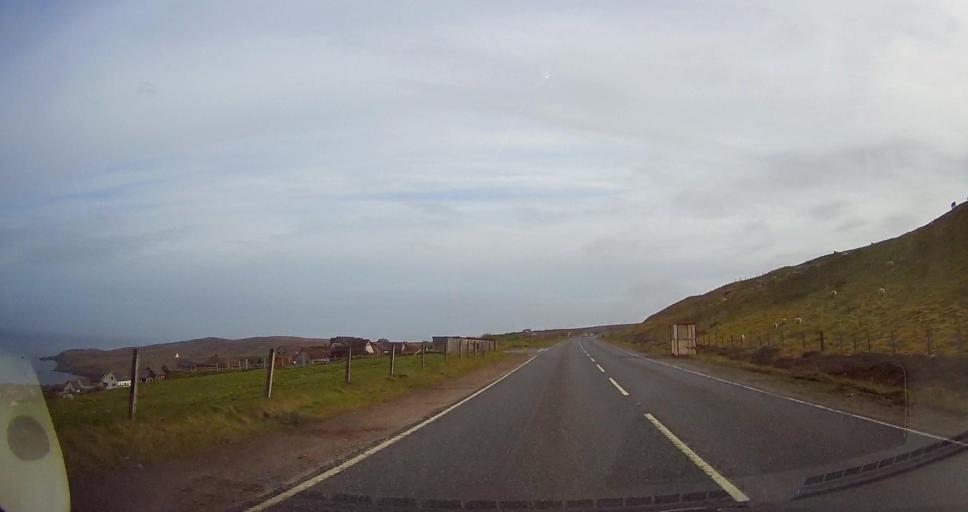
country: GB
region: Scotland
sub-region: Shetland Islands
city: Lerwick
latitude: 60.1312
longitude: -1.2149
